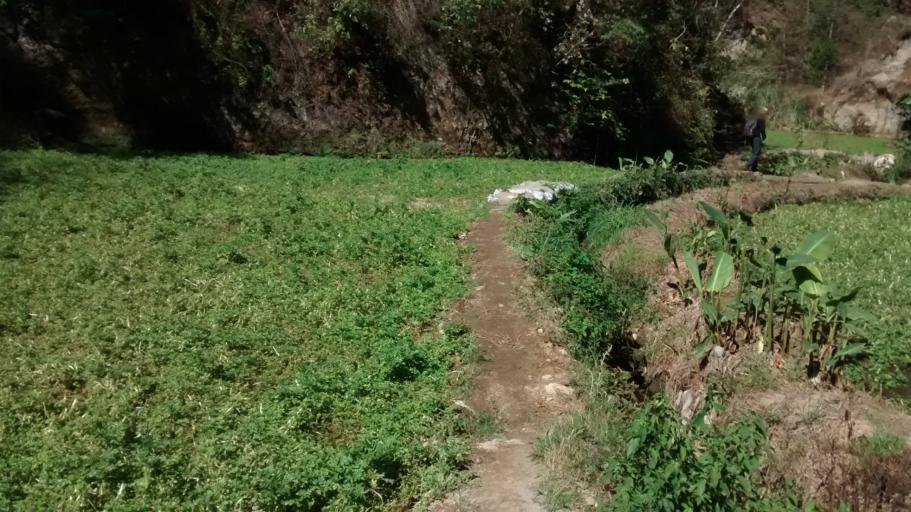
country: GT
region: Sacatepequez
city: Santo Domingo Xenacoj
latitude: 14.6810
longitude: -90.7236
